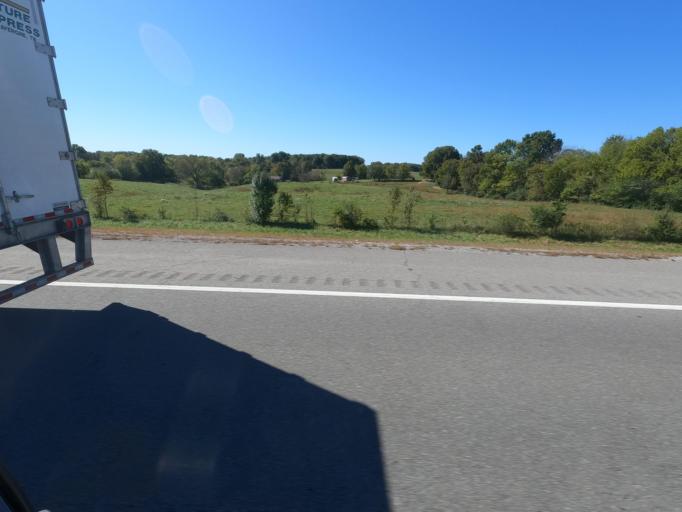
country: US
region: Tennessee
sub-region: Williamson County
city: Fairview
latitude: 35.9100
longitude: -87.1609
